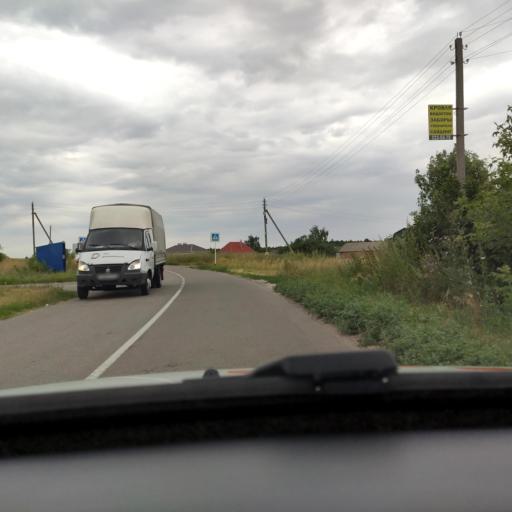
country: RU
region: Voronezj
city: Orlovo
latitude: 51.6750
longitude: 39.5739
